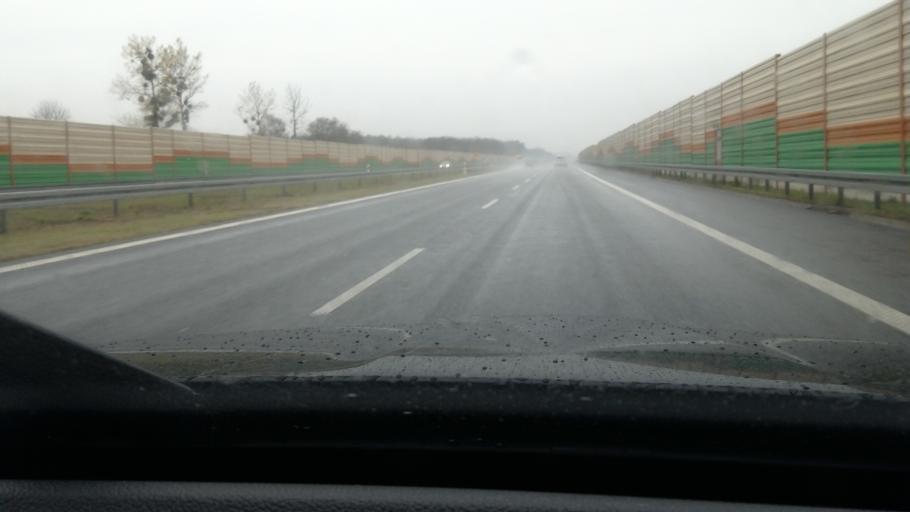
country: PL
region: Lodz Voivodeship
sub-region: Powiat skierniewicki
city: Bolimow
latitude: 52.0584
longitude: 20.1463
